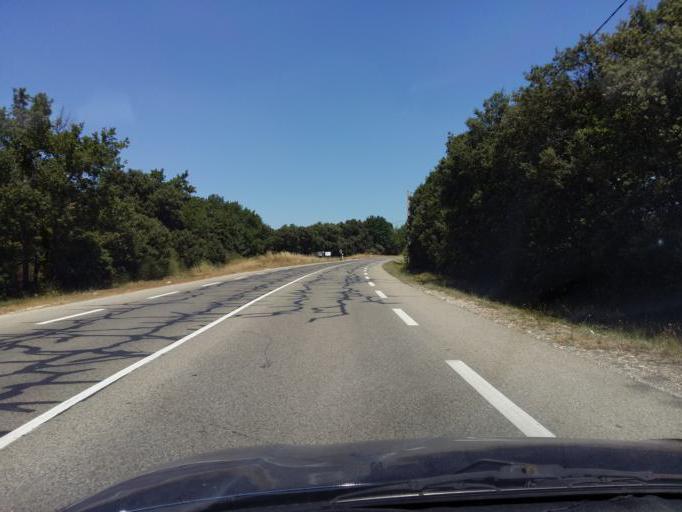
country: FR
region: Provence-Alpes-Cote d'Azur
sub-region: Departement du Vaucluse
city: Visan
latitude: 44.3409
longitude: 4.9490
